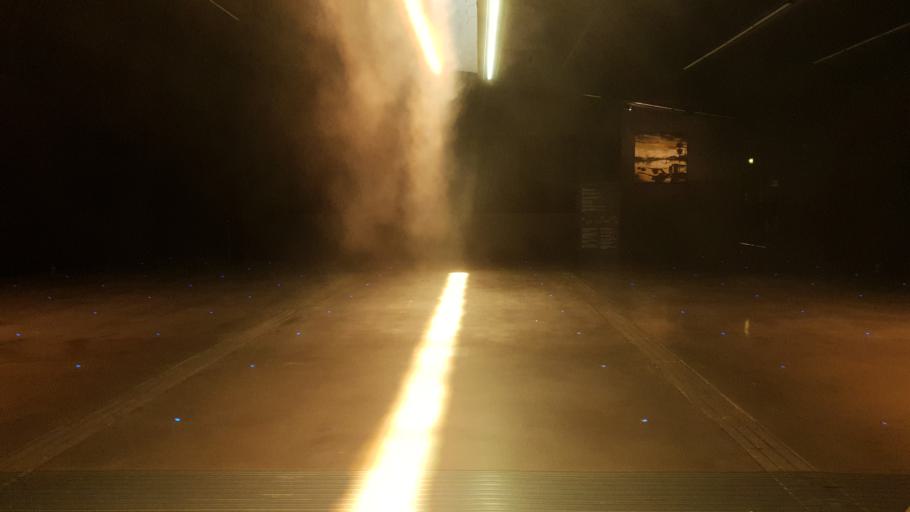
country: IT
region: Lombardy
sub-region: Provincia di Varese
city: Vizzola Ticino
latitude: 45.6272
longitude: 8.7118
